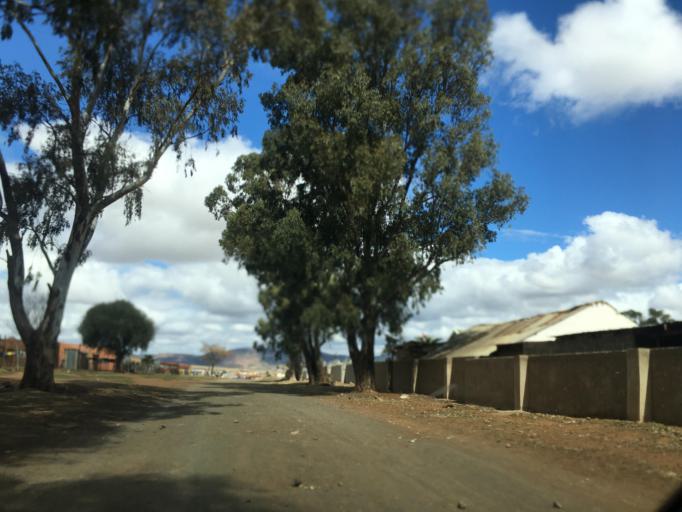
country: ZA
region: Eastern Cape
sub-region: Chris Hani District Municipality
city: Cala
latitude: -31.5293
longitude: 27.7033
